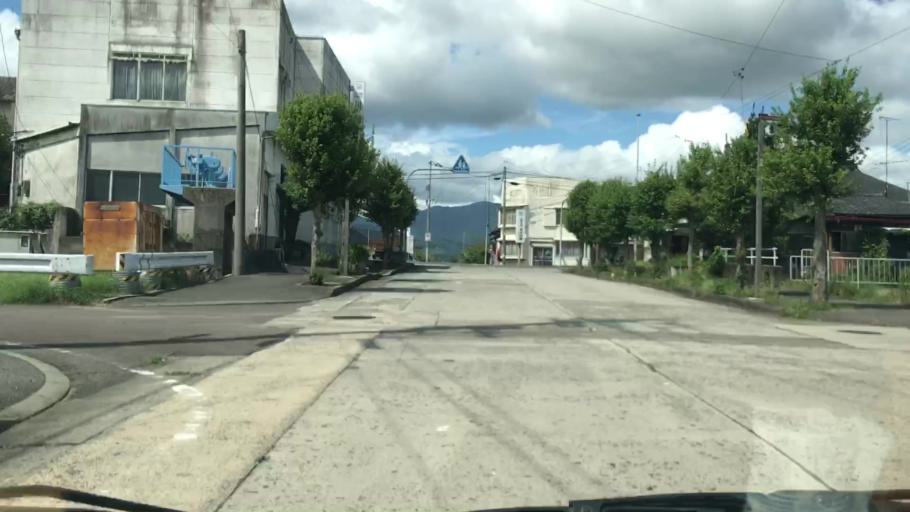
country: JP
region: Saga Prefecture
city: Saga-shi
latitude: 33.2489
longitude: 130.2009
